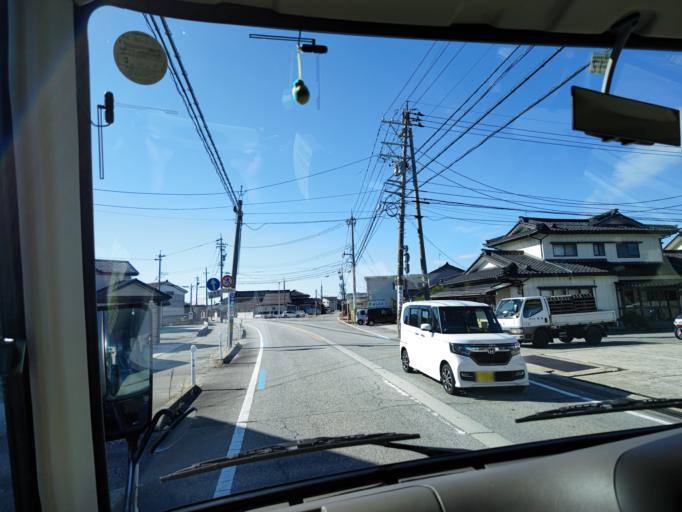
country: JP
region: Toyama
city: Nyuzen
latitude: 36.8981
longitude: 137.4202
